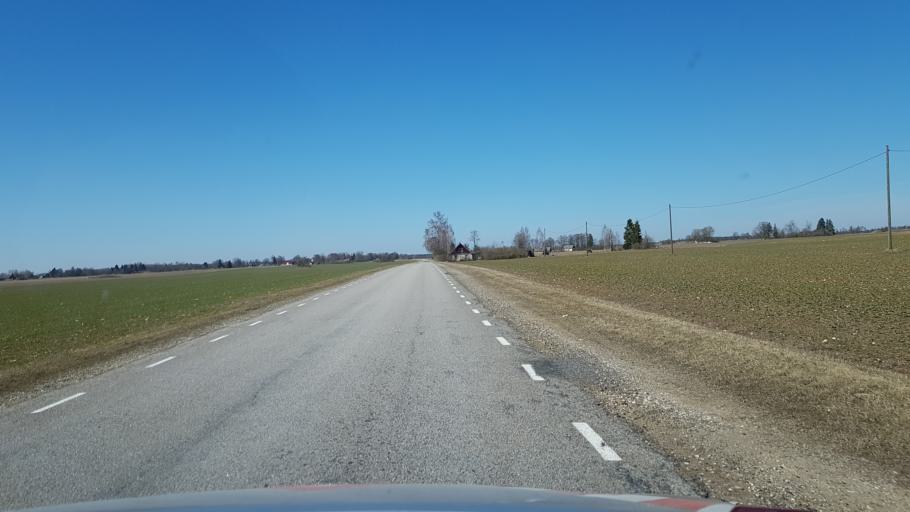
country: EE
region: Laeaene-Virumaa
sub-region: Vaeike-Maarja vald
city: Vaike-Maarja
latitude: 59.0990
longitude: 26.3972
